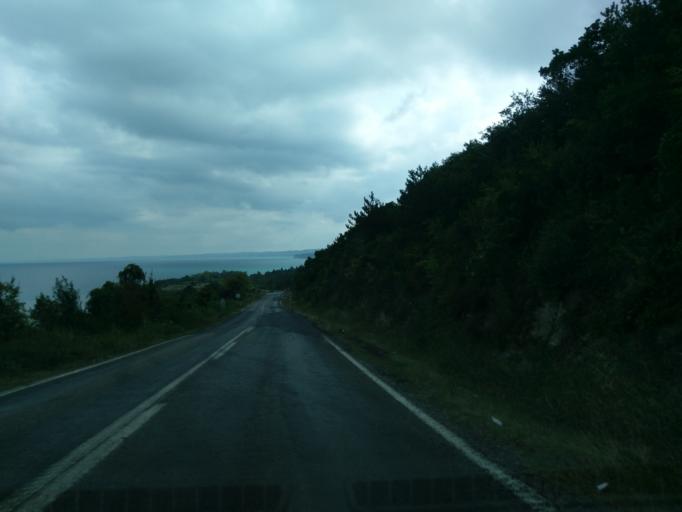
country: TR
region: Sinop
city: Ayancik
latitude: 41.9427
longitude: 34.6802
